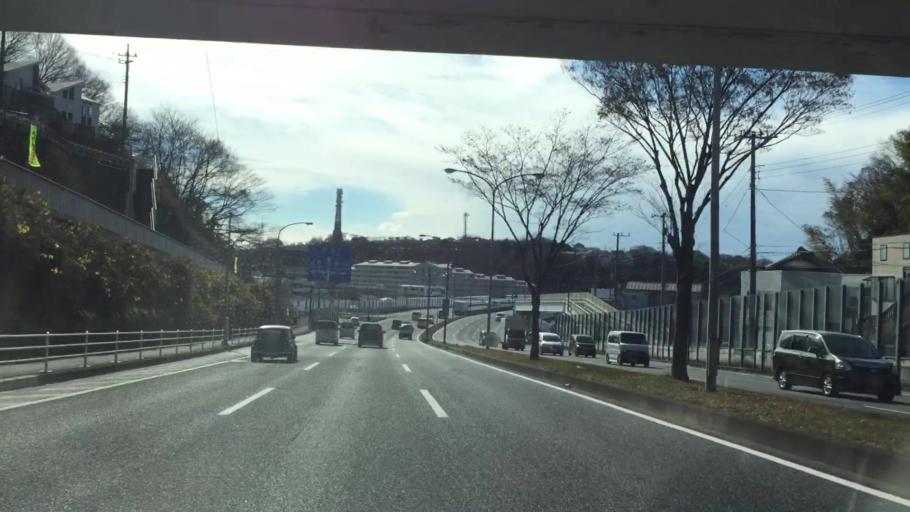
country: JP
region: Kanagawa
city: Yokohama
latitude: 35.4754
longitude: 139.5760
